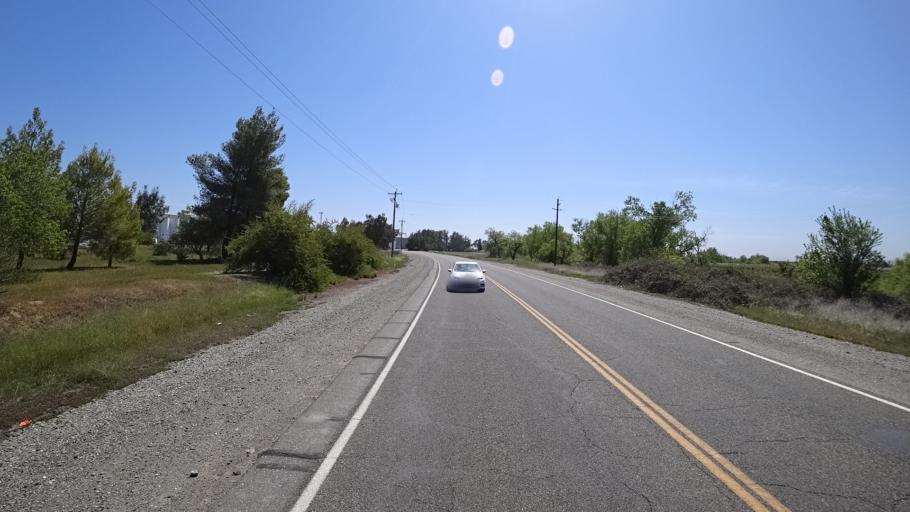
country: US
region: California
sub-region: Glenn County
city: Willows
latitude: 39.6261
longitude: -122.1969
